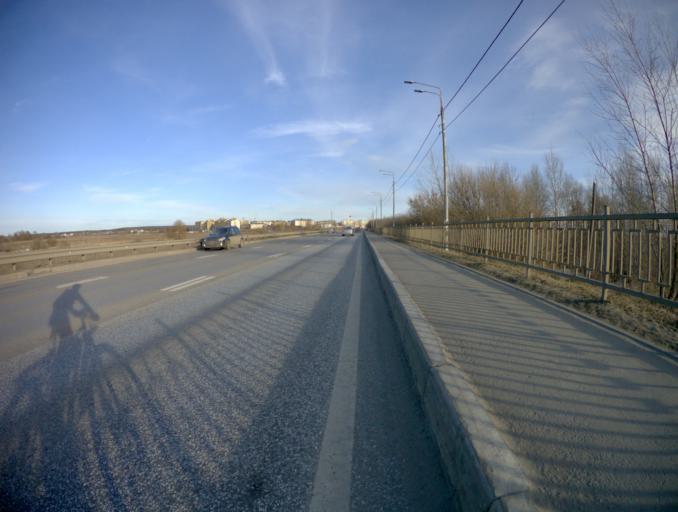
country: RU
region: Vladimir
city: Kommunar
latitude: 56.1150
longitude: 40.4215
